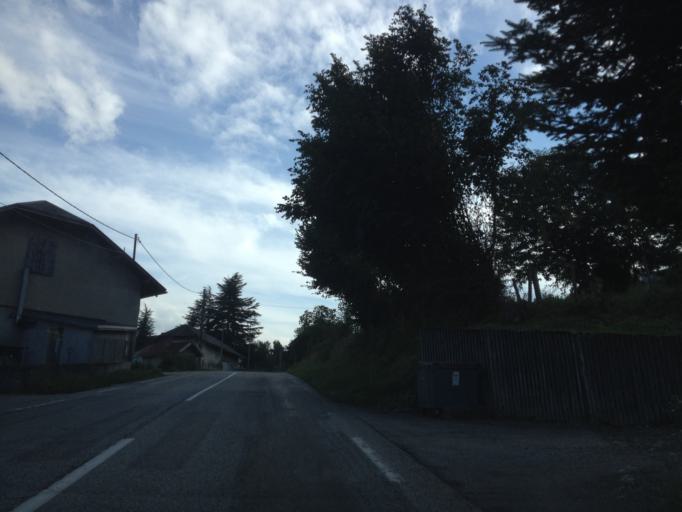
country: FR
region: Rhone-Alpes
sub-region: Departement de la Savoie
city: Le Bourget-du-Lac
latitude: 45.6406
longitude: 5.8630
